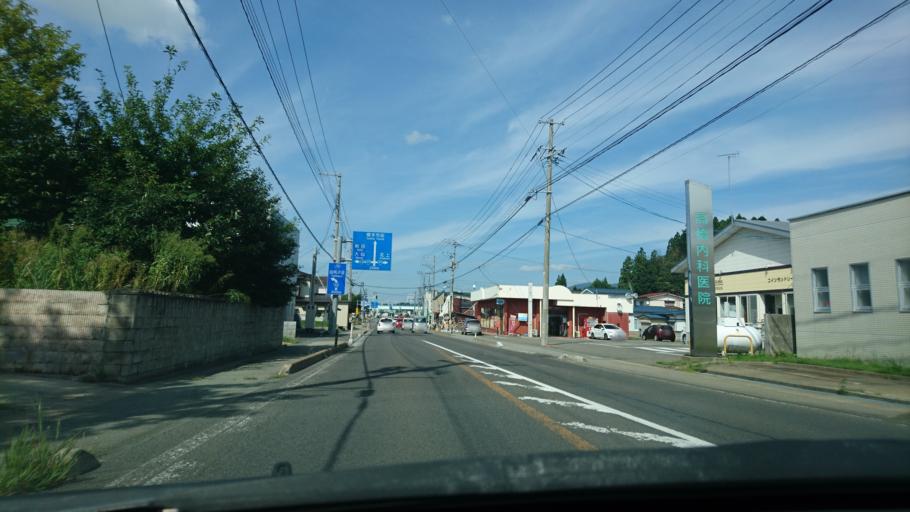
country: JP
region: Akita
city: Yokotemachi
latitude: 39.2957
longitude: 140.5632
